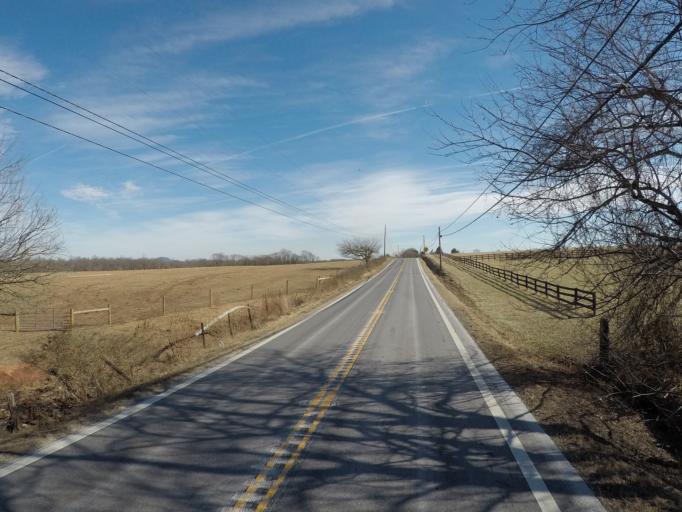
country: US
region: Maryland
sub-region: Frederick County
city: Point of Rocks
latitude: 39.2521
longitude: -77.5341
